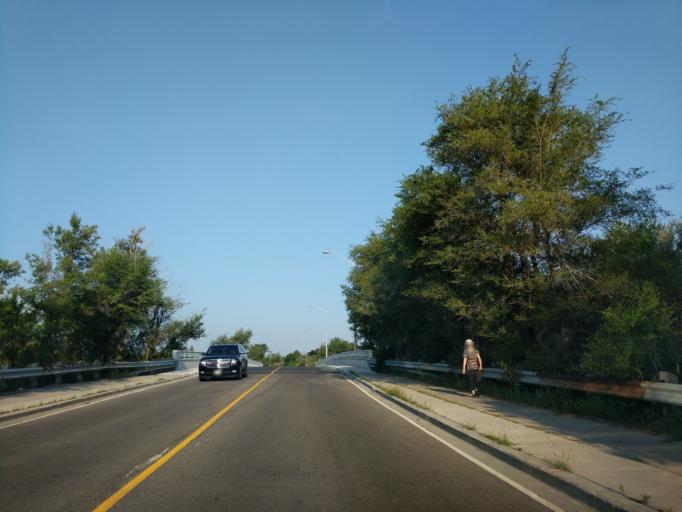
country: CA
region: Ontario
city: Willowdale
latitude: 43.8031
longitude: -79.3441
